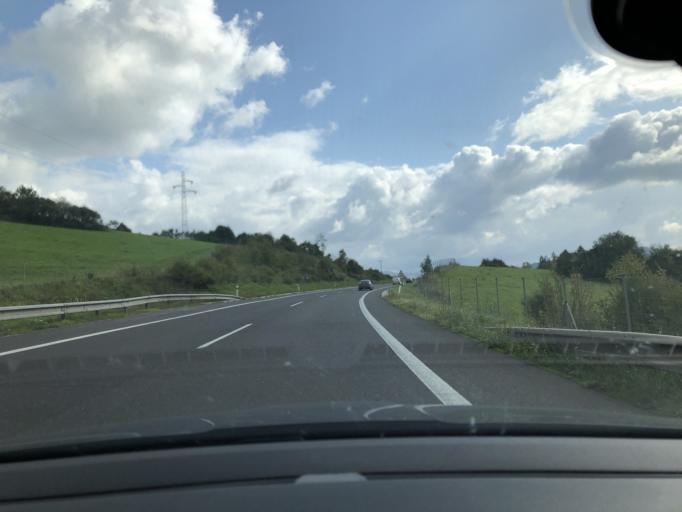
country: SK
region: Zilinsky
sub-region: Okres Dolny Kubin
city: Dolny Kubin
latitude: 49.2599
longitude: 19.3878
